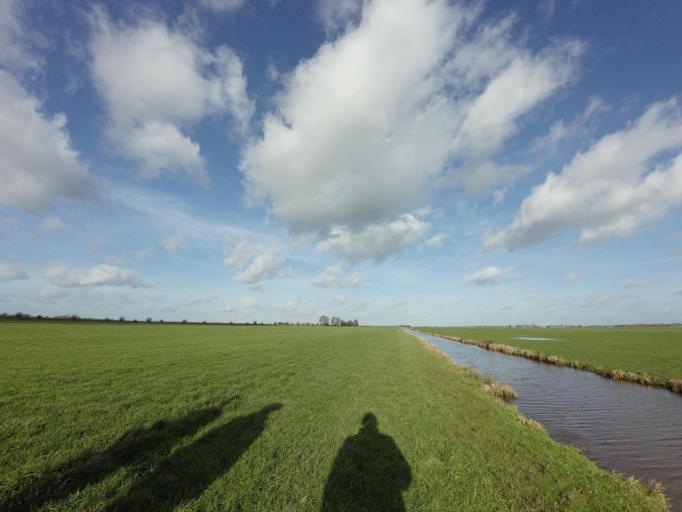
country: NL
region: Utrecht
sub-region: Gemeente Woerden
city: Woerden
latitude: 52.0979
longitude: 4.8716
